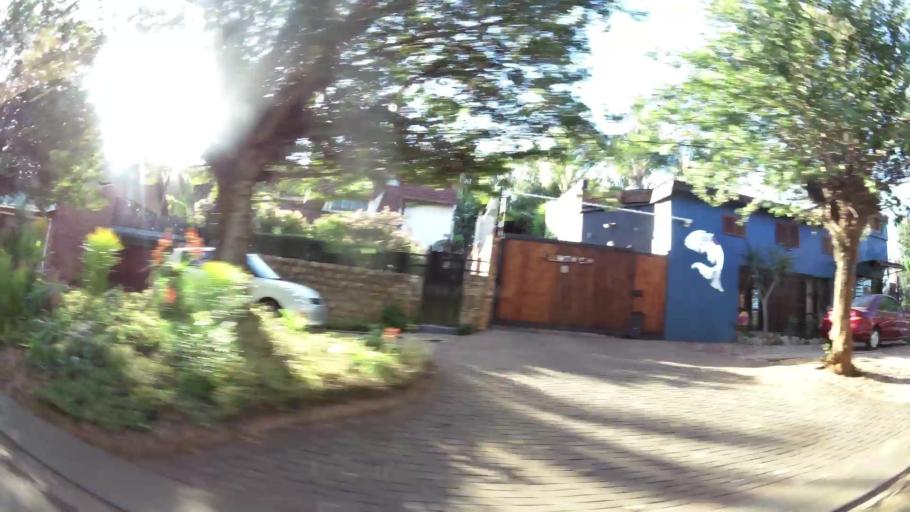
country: ZA
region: Gauteng
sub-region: City of Tshwane Metropolitan Municipality
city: Pretoria
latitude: -25.7301
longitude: 28.2076
